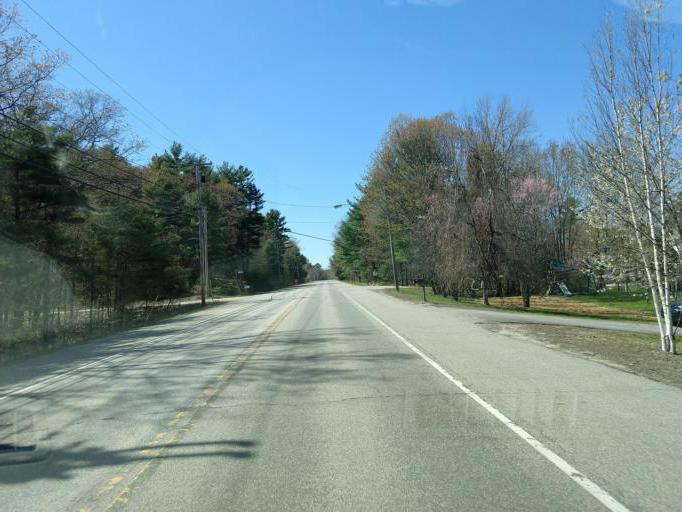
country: US
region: Maine
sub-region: York County
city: Saco
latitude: 43.4647
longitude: -70.4015
